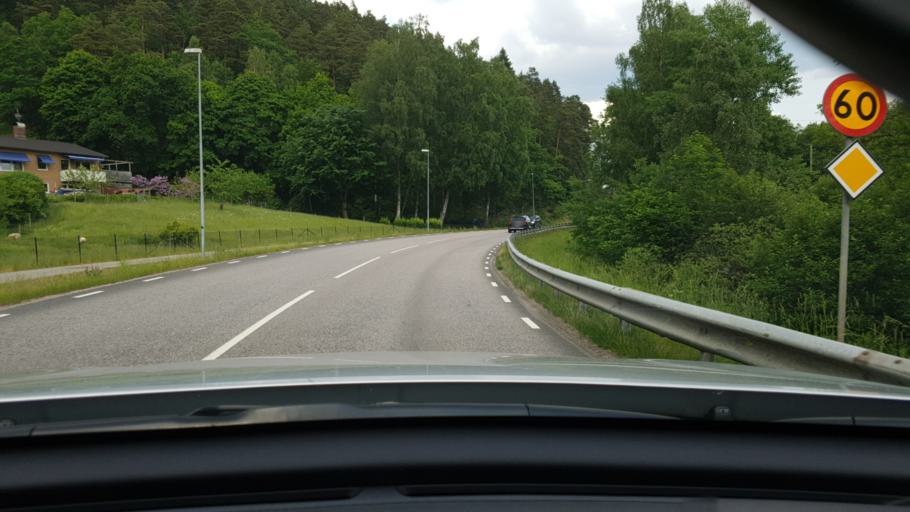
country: SE
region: Vaestra Goetaland
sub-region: Lerums Kommun
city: Stenkullen
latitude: 57.8016
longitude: 12.3368
